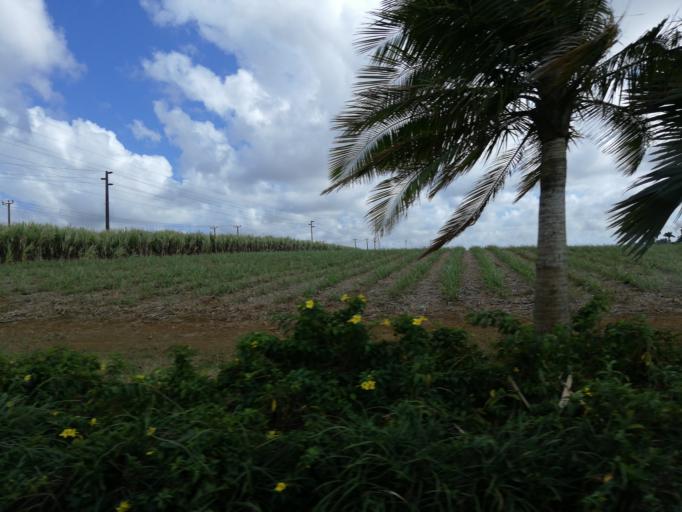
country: MU
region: Flacq
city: Queen Victoria
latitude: -20.2204
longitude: 57.6906
